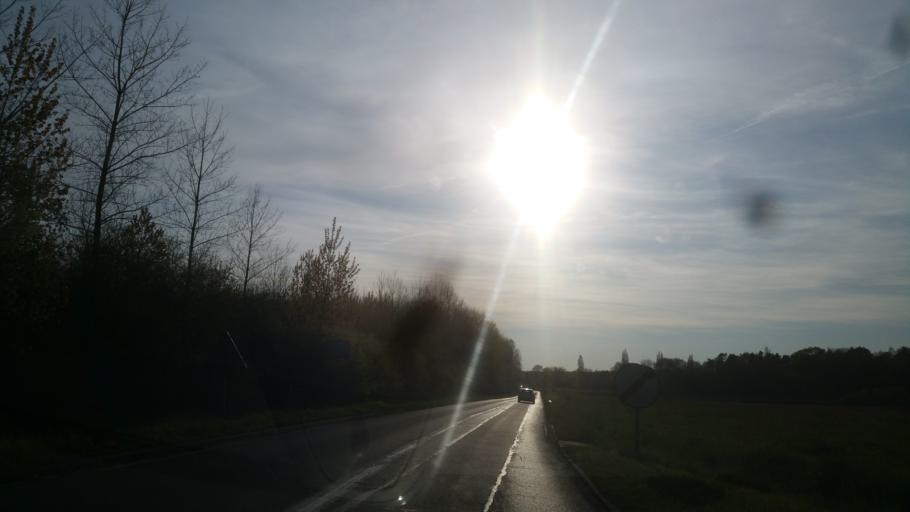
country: FR
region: Ile-de-France
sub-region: Departement de l'Essonne
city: Saint-Maurice-Montcouronne
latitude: 48.5774
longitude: 2.1380
